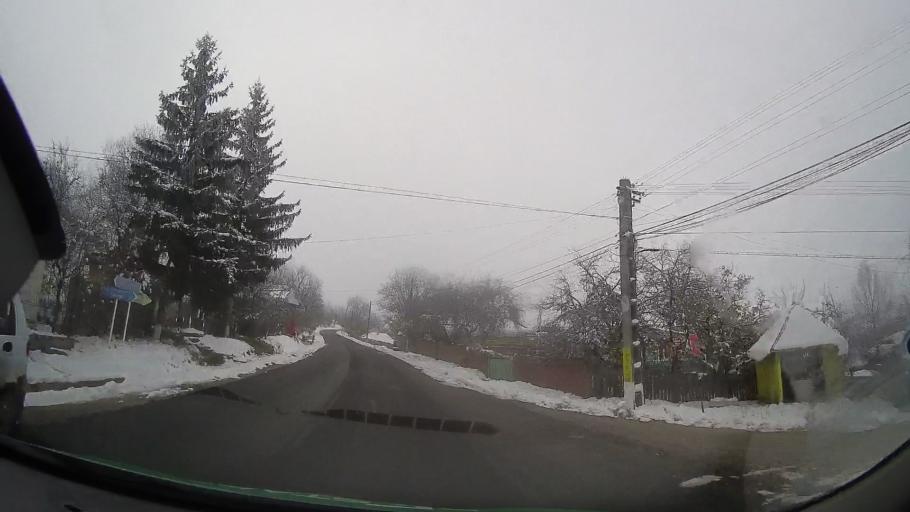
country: RO
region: Bacau
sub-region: Comuna Oncesti
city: Oncesti
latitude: 46.4714
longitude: 27.2559
